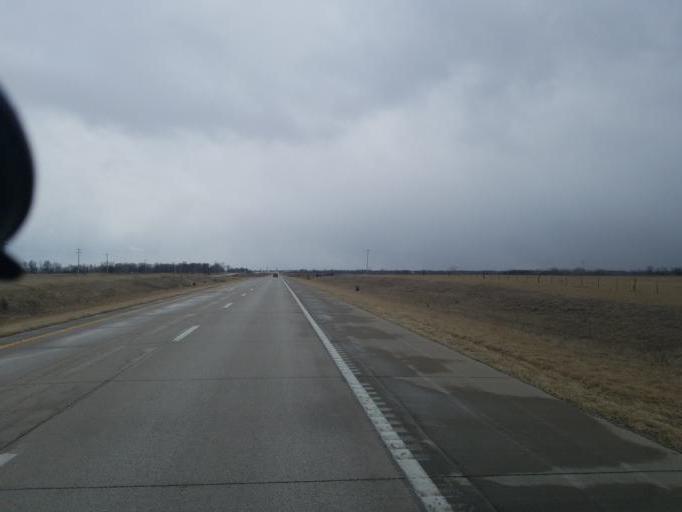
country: US
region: Missouri
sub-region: Randolph County
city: Moberly
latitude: 39.4852
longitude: -92.4345
